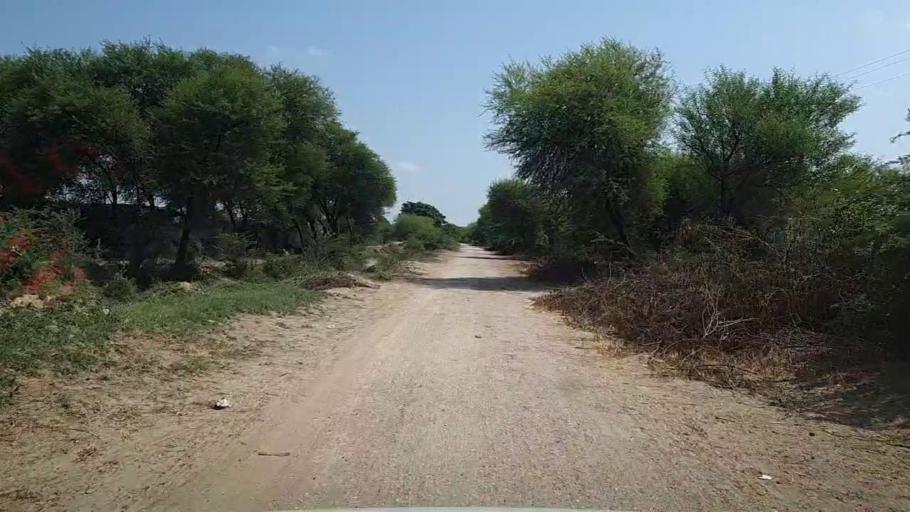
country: PK
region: Sindh
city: Kario
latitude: 24.8527
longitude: 68.6876
